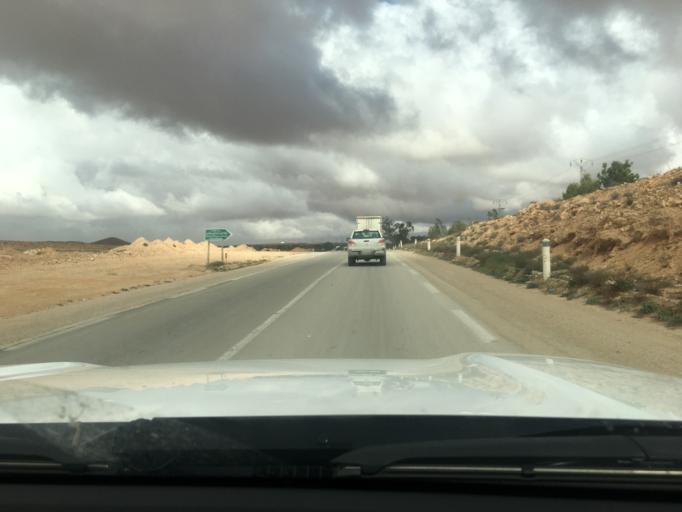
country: TN
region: Tataouine
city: Tataouine
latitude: 33.0771
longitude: 10.4920
